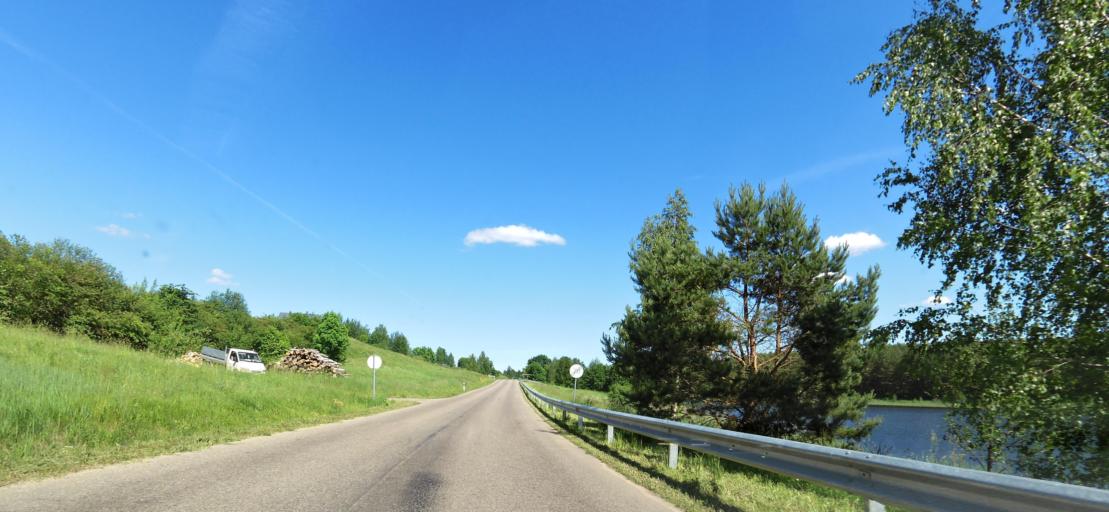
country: LT
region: Utenos apskritis
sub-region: Anyksciai
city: Anyksciai
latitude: 55.3200
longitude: 25.1147
